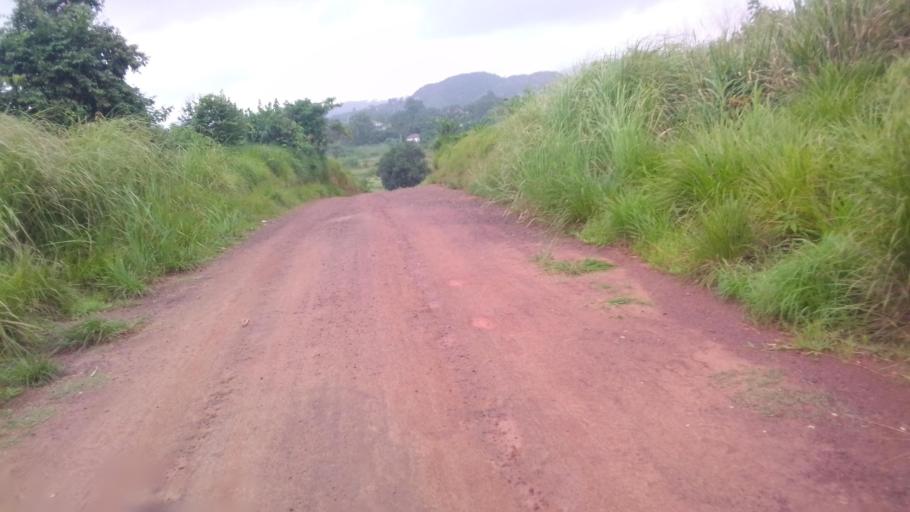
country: SL
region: Eastern Province
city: Kenema
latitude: 7.8405
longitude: -11.1773
